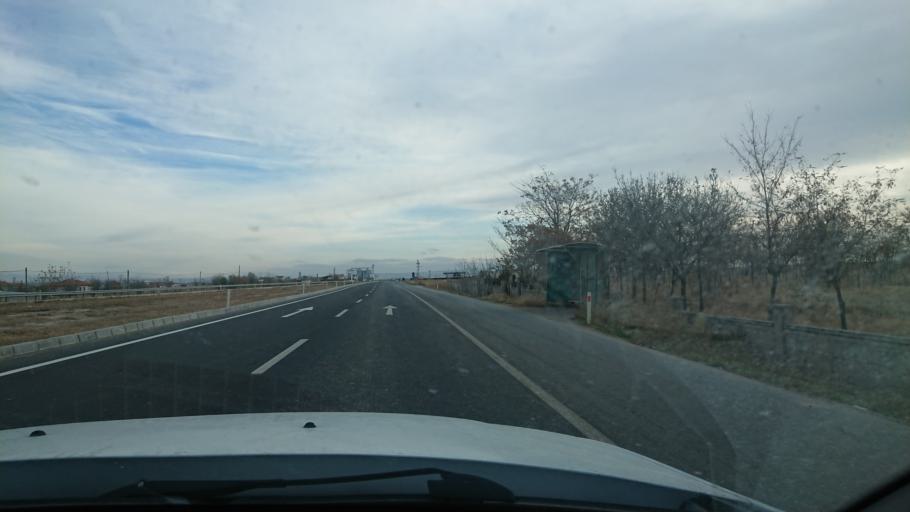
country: TR
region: Aksaray
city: Yesilova
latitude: 38.3255
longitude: 33.8832
